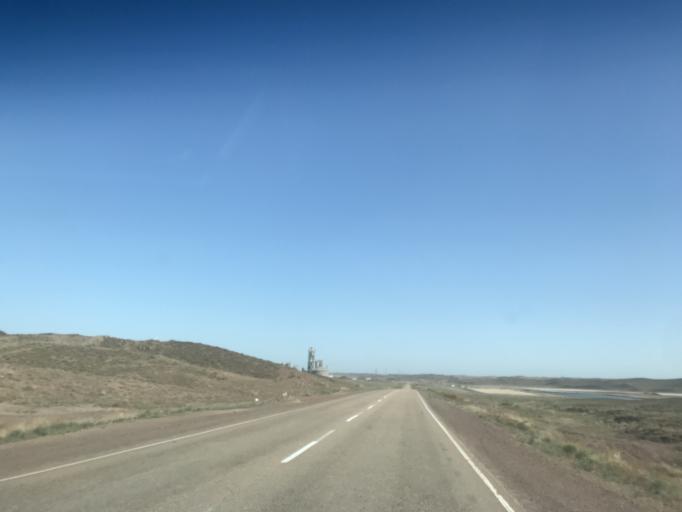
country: KZ
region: Zhambyl
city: Mynaral
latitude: 45.4020
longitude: 73.6370
